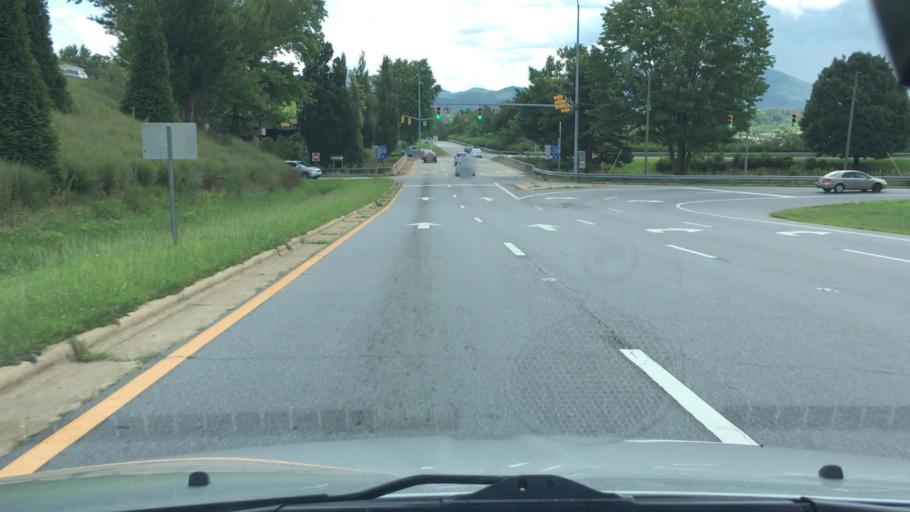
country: US
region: North Carolina
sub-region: Buncombe County
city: Asheville
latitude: 35.5860
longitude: -82.5238
